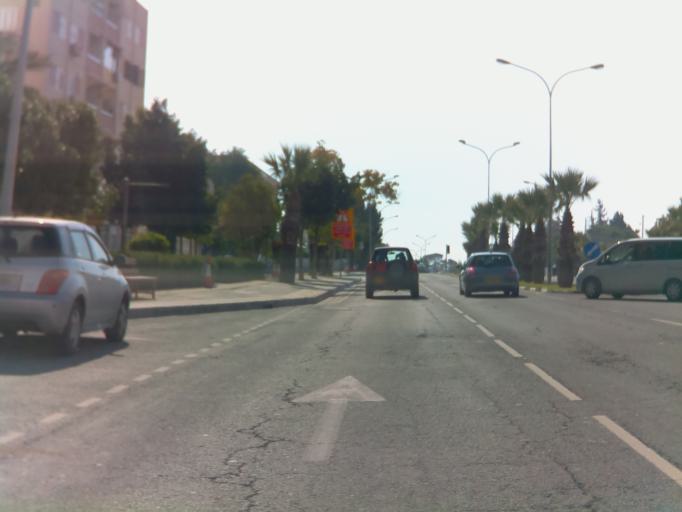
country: CY
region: Larnaka
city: Larnaca
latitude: 34.9023
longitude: 33.6304
